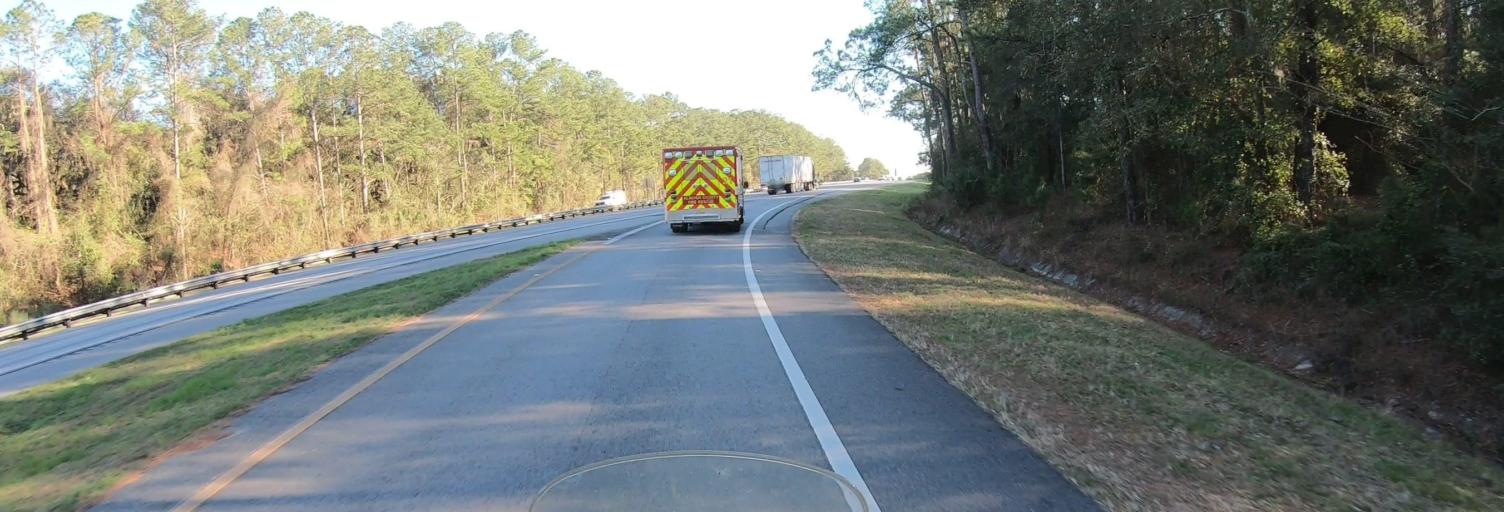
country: US
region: Florida
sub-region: Alachua County
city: High Springs
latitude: 29.8708
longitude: -82.5430
